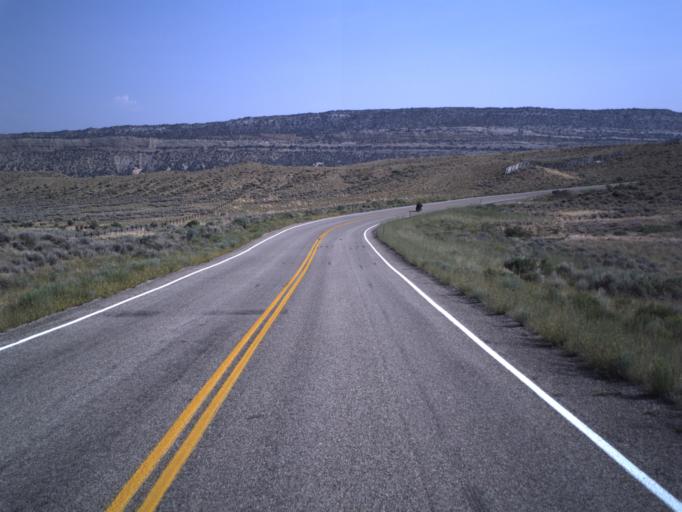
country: US
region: Utah
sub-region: Daggett County
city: Manila
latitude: 40.9726
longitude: -109.4635
